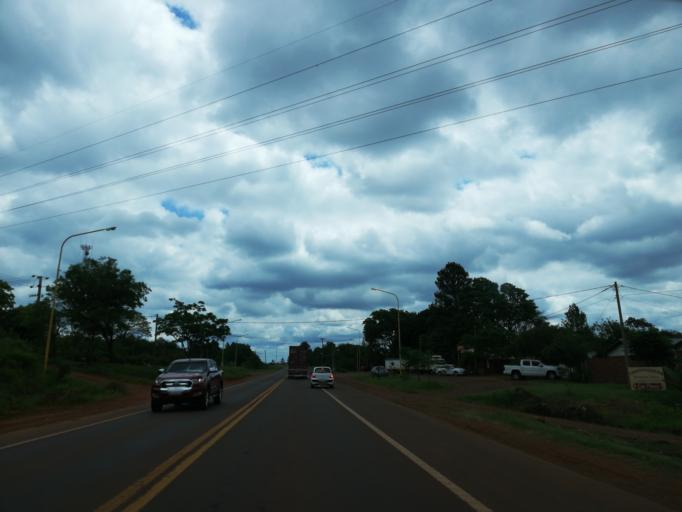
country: AR
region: Misiones
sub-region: Departamento de Leandro N. Alem
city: Leandro N. Alem
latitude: -27.6164
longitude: -55.3075
